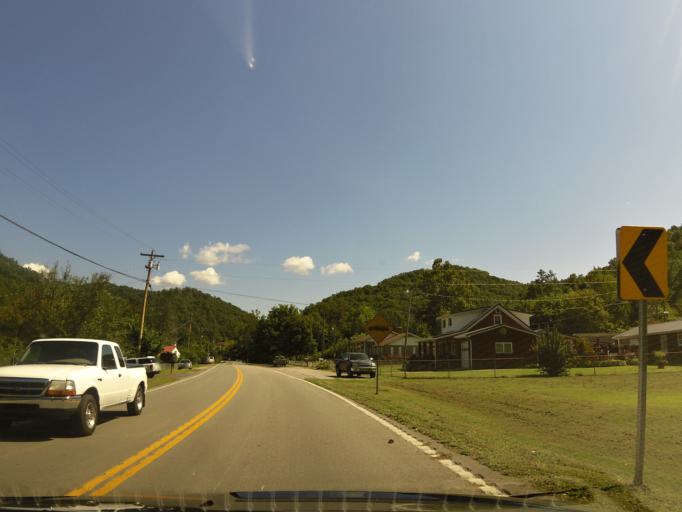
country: US
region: Kentucky
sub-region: Clay County
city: Manchester
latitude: 37.1594
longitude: -83.5679
